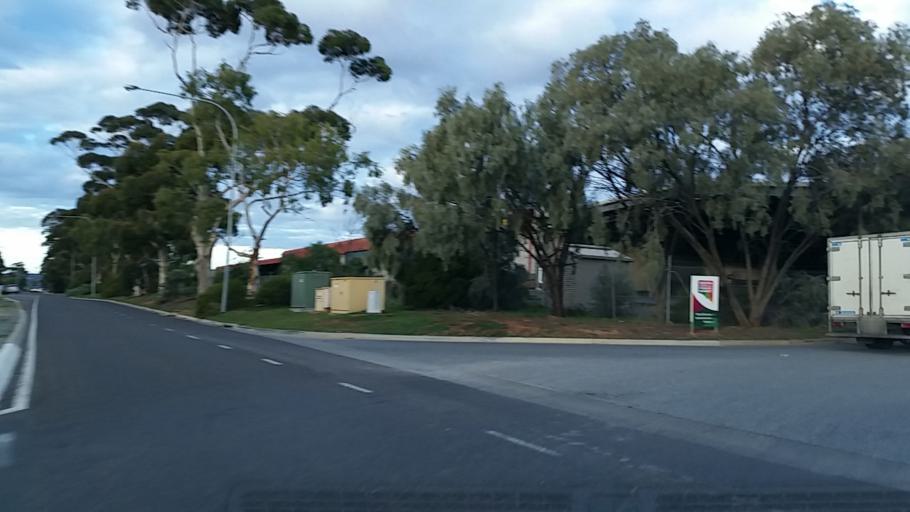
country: AU
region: South Australia
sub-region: Port Adelaide Enfield
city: Enfield
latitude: -34.8303
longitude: 138.6048
